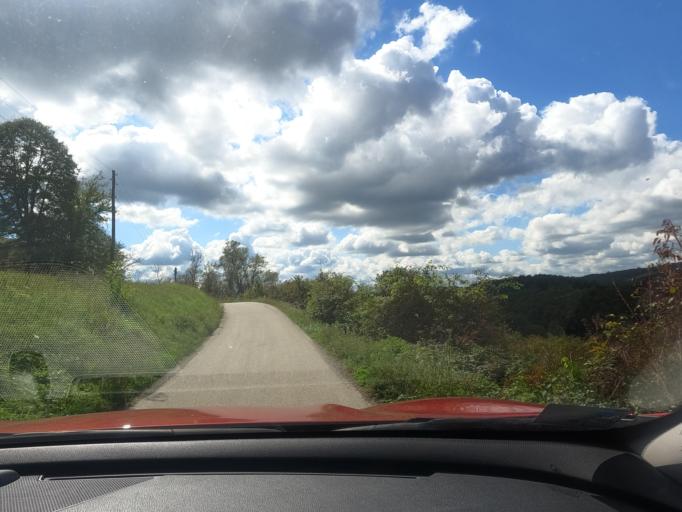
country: HR
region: Karlovacka
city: Vojnic
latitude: 45.2294
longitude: 15.7078
